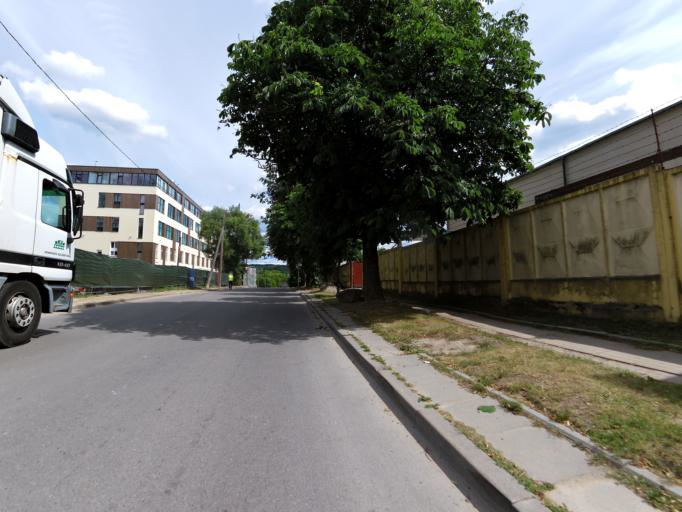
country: LT
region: Vilnius County
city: Rasos
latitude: 54.6774
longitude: 25.3175
